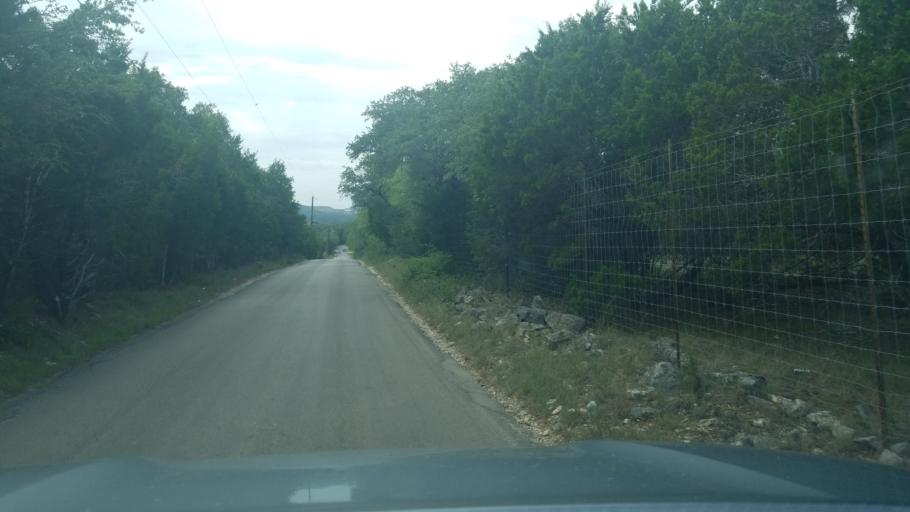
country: US
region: Texas
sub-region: Comal County
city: Bulverde
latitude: 29.7639
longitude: -98.4089
